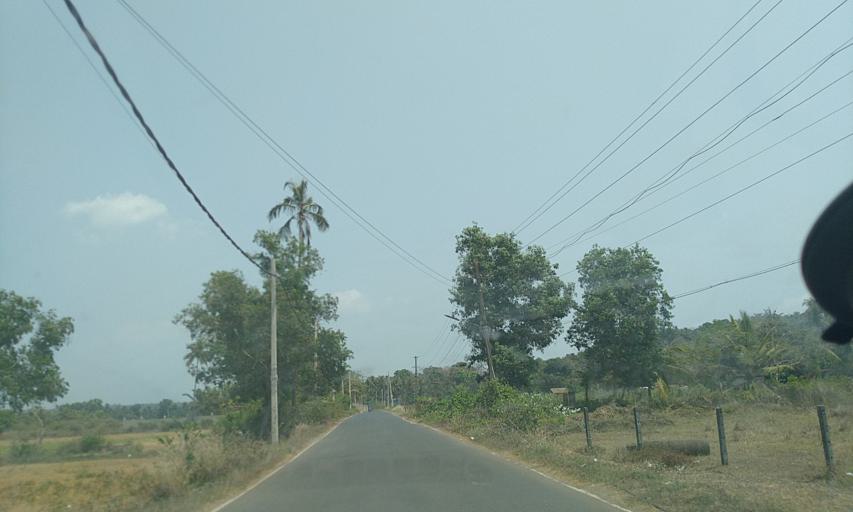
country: IN
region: Goa
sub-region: North Goa
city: Saligao
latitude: 15.5530
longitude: 73.8092
